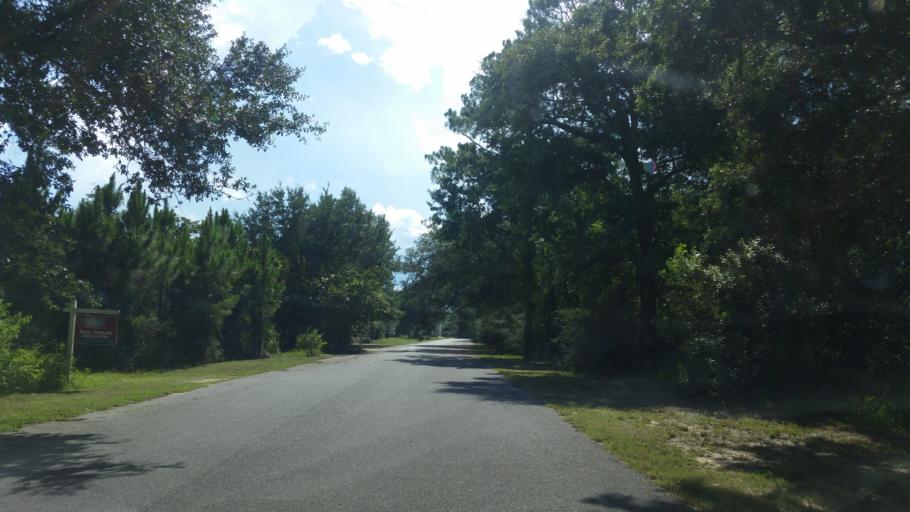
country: US
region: Florida
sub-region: Santa Rosa County
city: Pace
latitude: 30.5816
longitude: -87.1697
